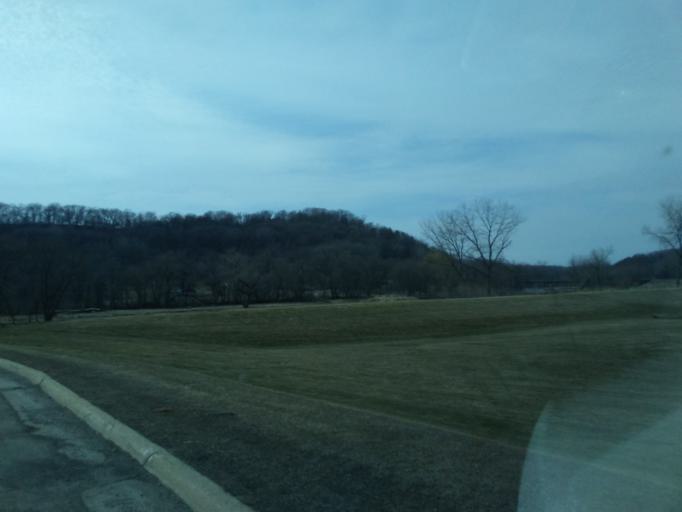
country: US
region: Iowa
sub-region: Winneshiek County
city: Decorah
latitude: 43.3132
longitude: -91.8093
